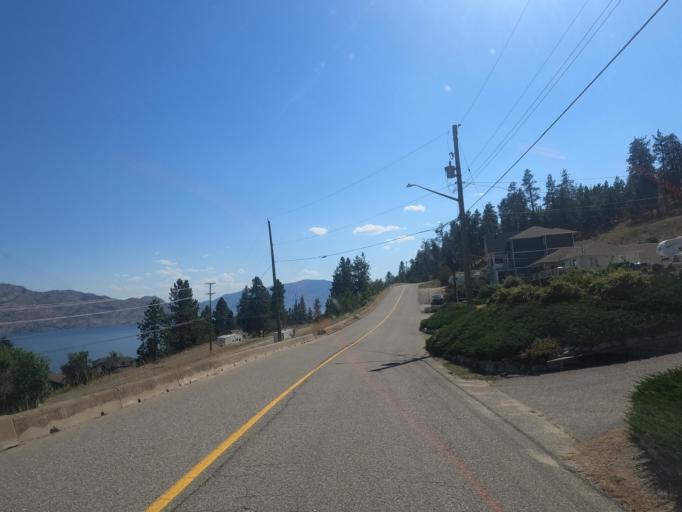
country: CA
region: British Columbia
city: Peachland
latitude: 49.7901
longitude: -119.7075
